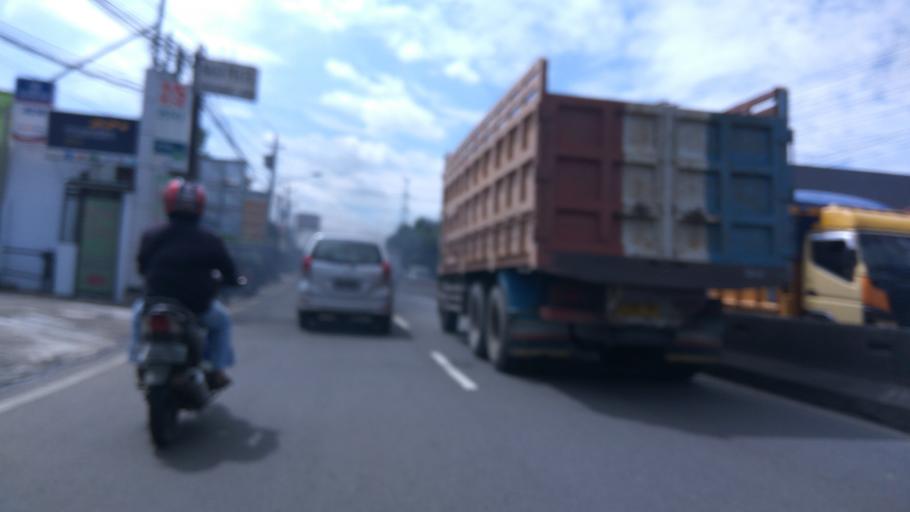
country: ID
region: Central Java
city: Ungaran
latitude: -7.1521
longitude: 110.4094
